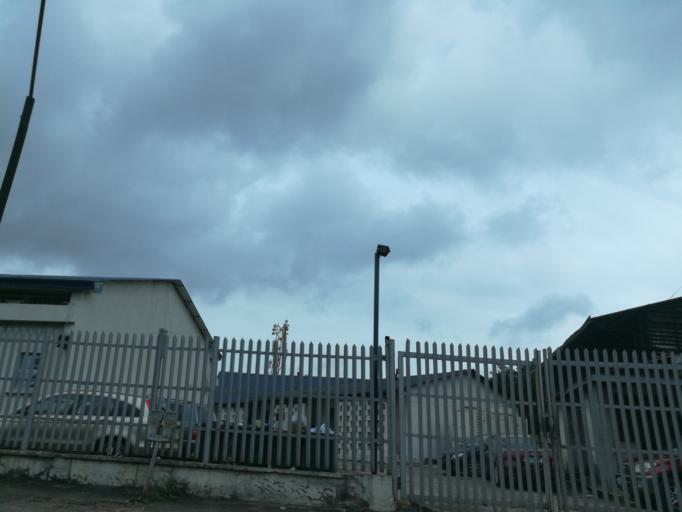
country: NG
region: Lagos
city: Ikeja
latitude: 6.6051
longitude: 3.3379
